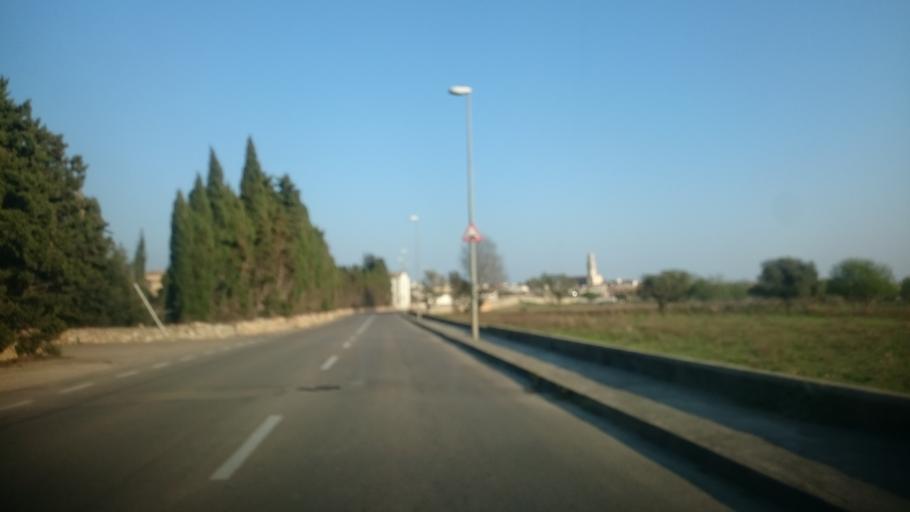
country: ES
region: Catalonia
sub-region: Provincia de Barcelona
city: Cubelles
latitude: 41.2124
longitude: 1.6673
